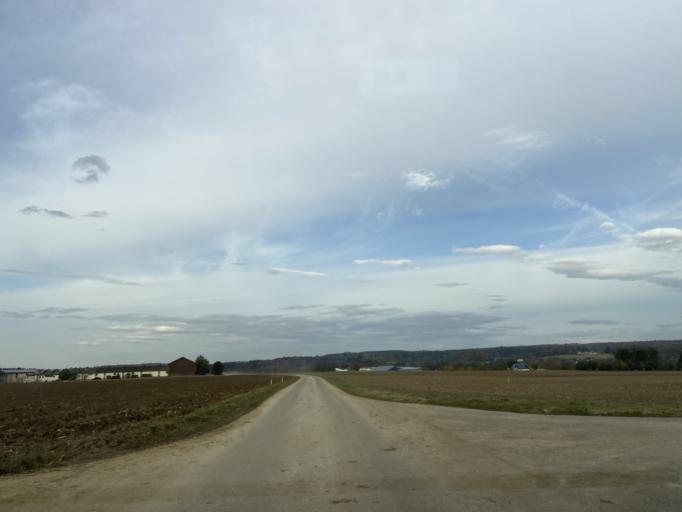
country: DE
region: Baden-Wuerttemberg
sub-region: Tuebingen Region
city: Bingen
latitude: 48.1023
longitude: 9.2739
